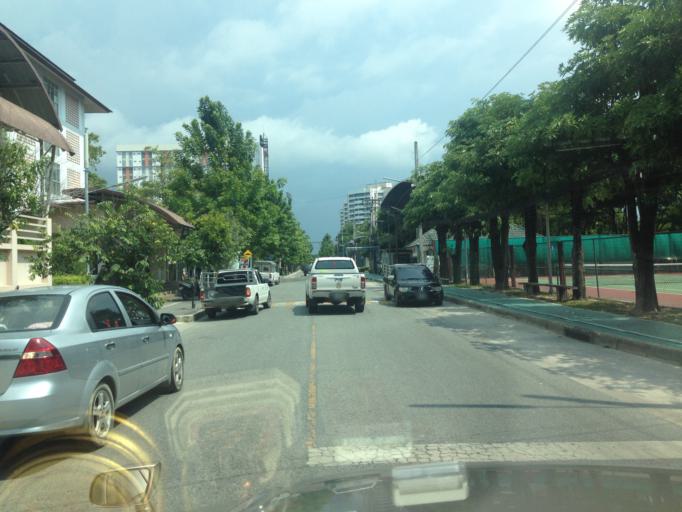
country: TH
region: Chon Buri
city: Chon Buri
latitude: 13.2766
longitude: 100.9280
